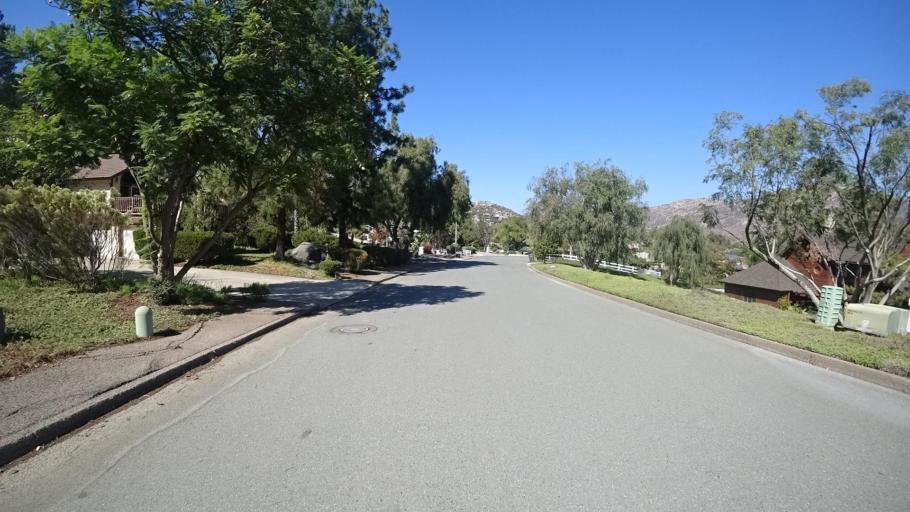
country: US
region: California
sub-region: San Diego County
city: Granite Hills
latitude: 32.7718
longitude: -116.8875
